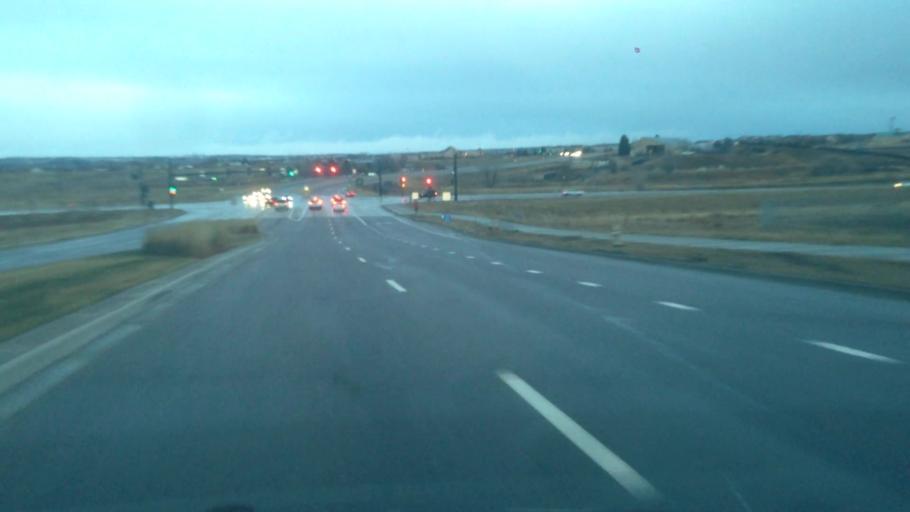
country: US
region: Colorado
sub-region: Douglas County
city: Stonegate
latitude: 39.5172
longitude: -104.8157
